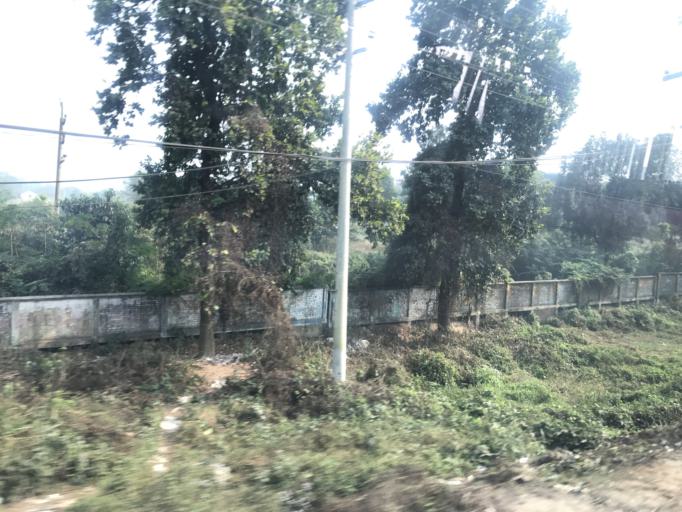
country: BD
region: Dhaka
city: Tungi
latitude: 23.8911
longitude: 90.2720
